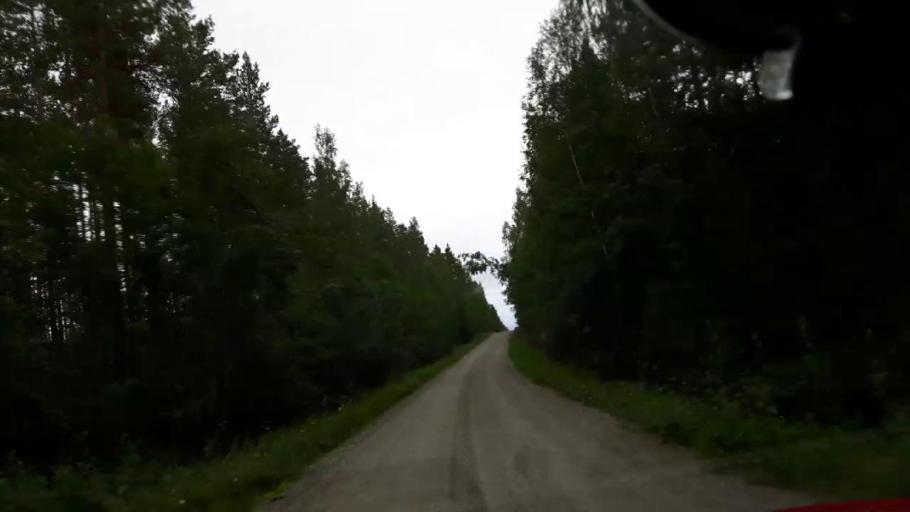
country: SE
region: Vaesternorrland
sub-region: Ange Kommun
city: Ange
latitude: 62.7915
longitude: 15.7733
